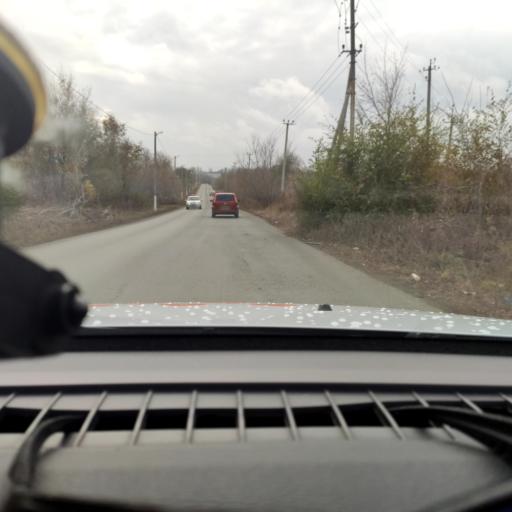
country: RU
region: Samara
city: Chapayevsk
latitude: 52.9925
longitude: 49.7311
